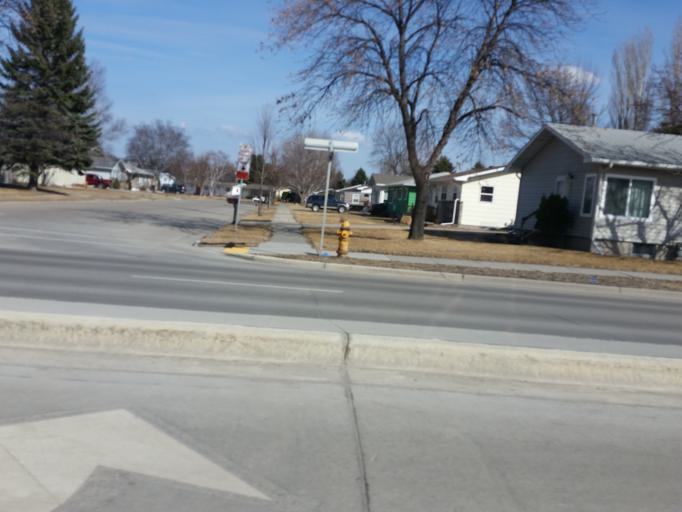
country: US
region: North Dakota
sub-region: Grand Forks County
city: Grand Forks
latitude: 47.9120
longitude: -97.0664
